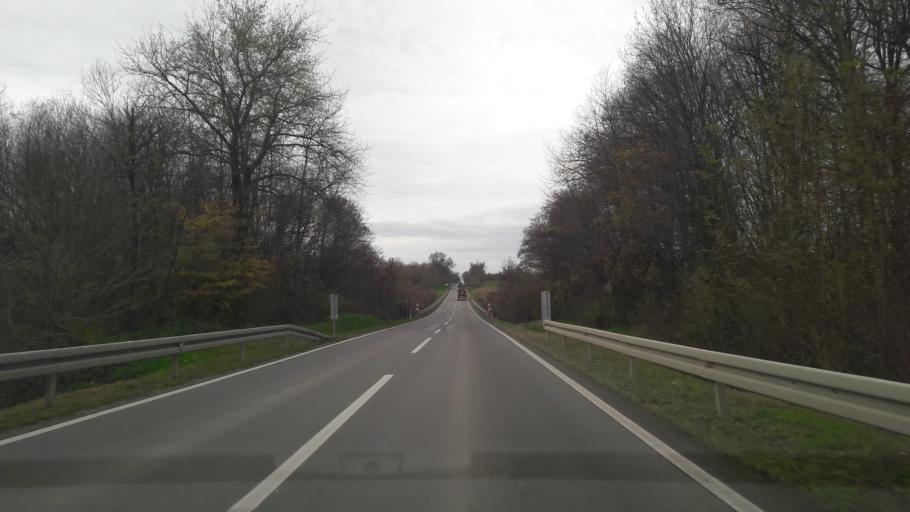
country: HR
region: Osjecko-Baranjska
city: Fericanci
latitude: 45.5369
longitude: 17.9331
